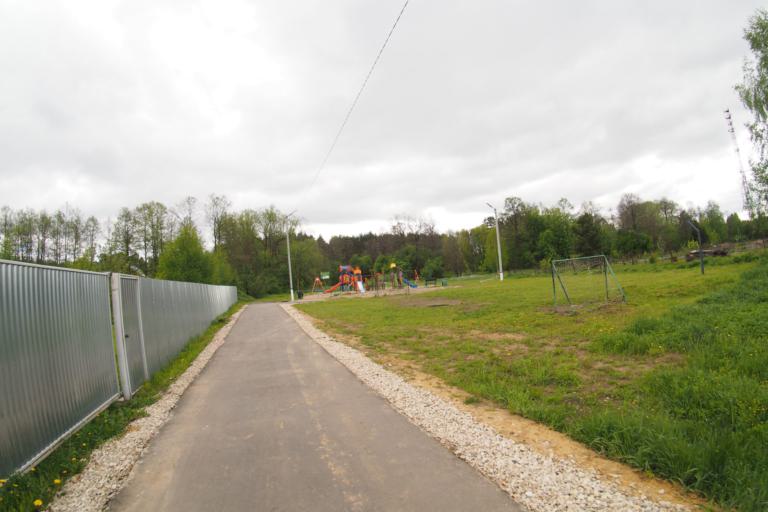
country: RU
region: Moskovskaya
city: Rechitsy
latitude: 55.5398
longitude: 38.4304
